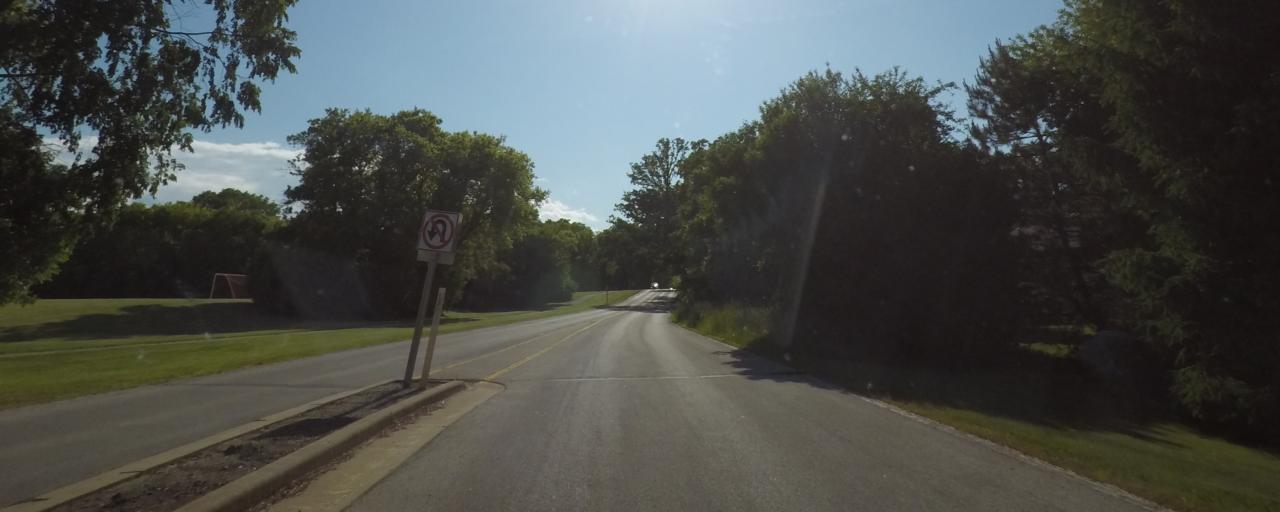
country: US
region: Wisconsin
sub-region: Milwaukee County
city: Greenfield
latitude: 42.9448
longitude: -88.0195
